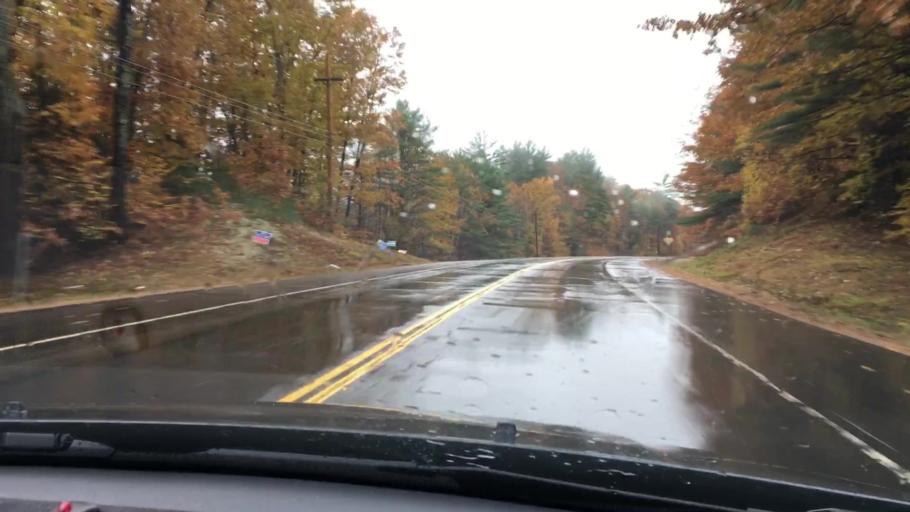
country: US
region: New Hampshire
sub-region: Grafton County
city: Ashland
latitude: 43.7113
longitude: -71.6258
